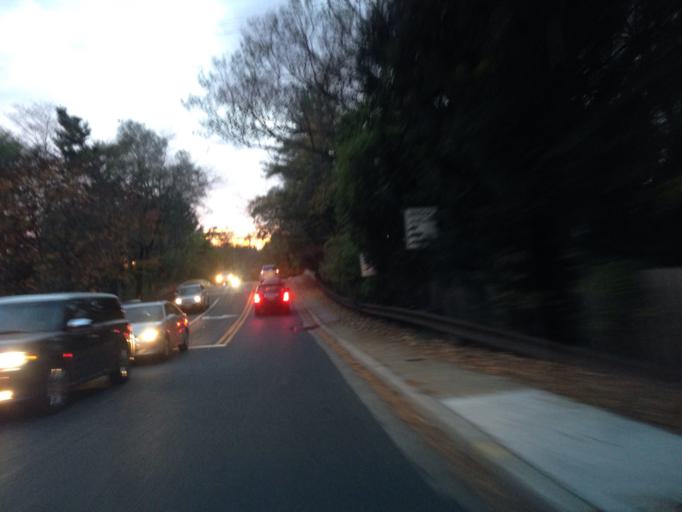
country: US
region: Maryland
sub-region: Baltimore County
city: Lutherville
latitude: 39.4092
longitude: -76.6443
